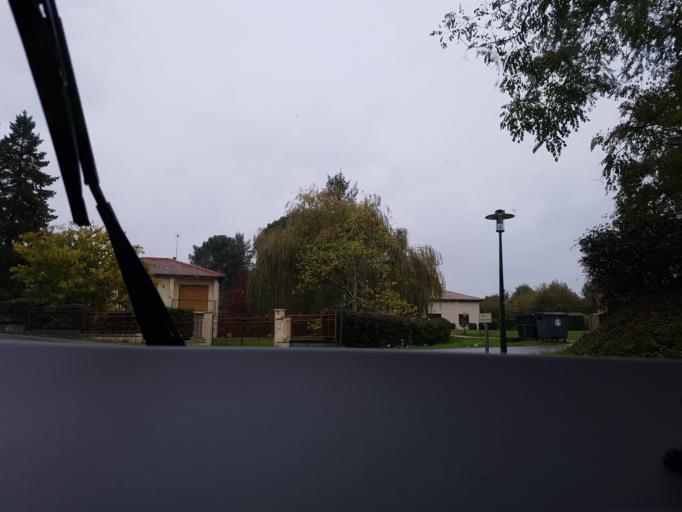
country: FR
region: Aquitaine
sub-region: Departement de la Gironde
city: Saint-Symphorien
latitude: 44.3304
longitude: -0.5866
